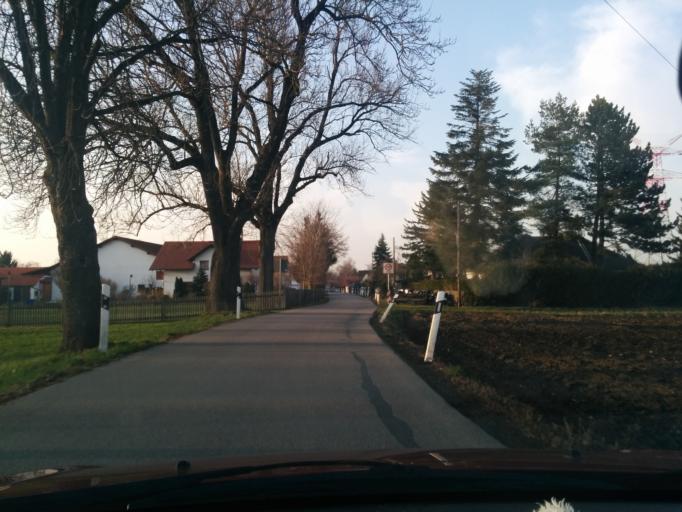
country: DE
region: Bavaria
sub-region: Upper Bavaria
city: Pasing
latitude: 48.1789
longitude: 11.4253
